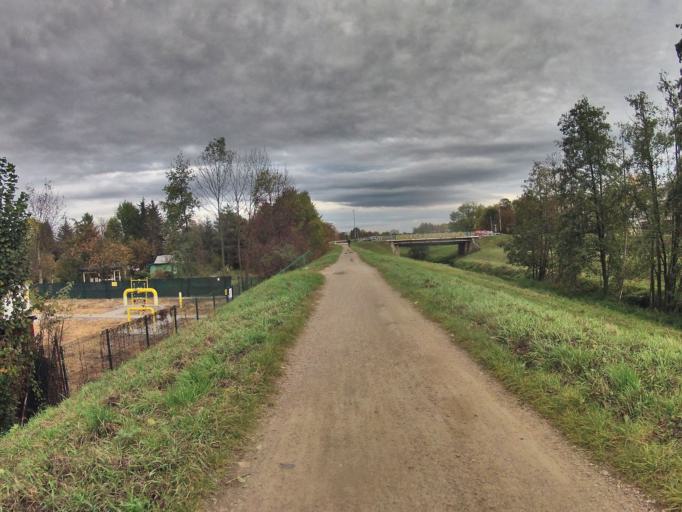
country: PL
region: Lesser Poland Voivodeship
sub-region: Krakow
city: Krakow
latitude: 50.0608
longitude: 19.8994
